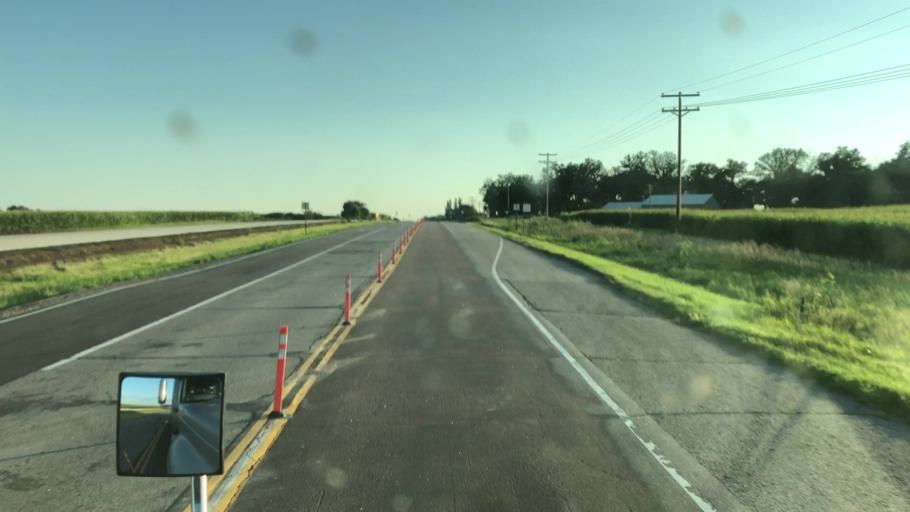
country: US
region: Minnesota
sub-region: Scott County
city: Belle Plaine
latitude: 44.5932
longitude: -93.8167
